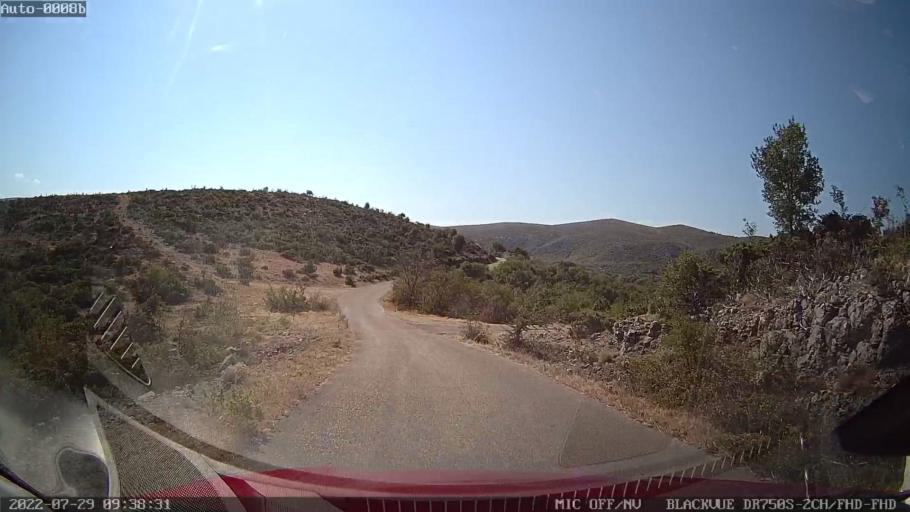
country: HR
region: Zadarska
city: Obrovac
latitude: 44.1979
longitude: 15.7502
